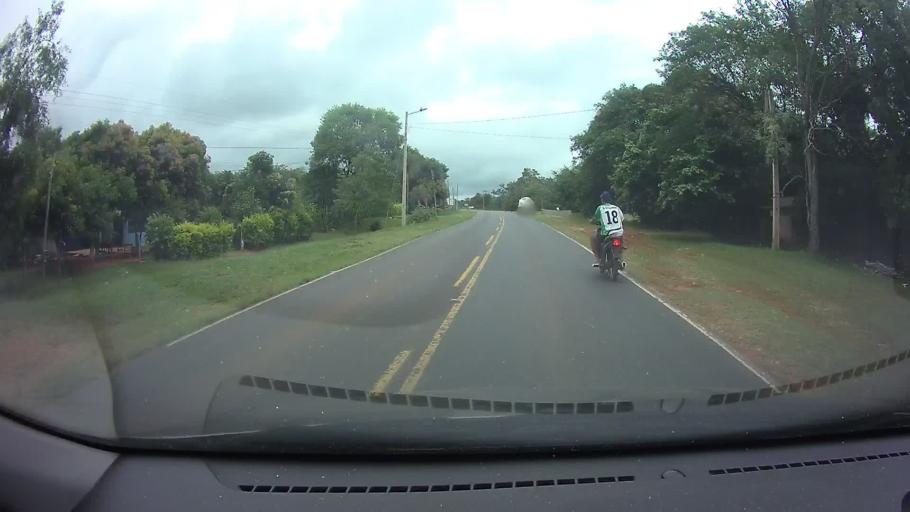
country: PY
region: Central
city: Guarambare
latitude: -25.5104
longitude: -57.4876
